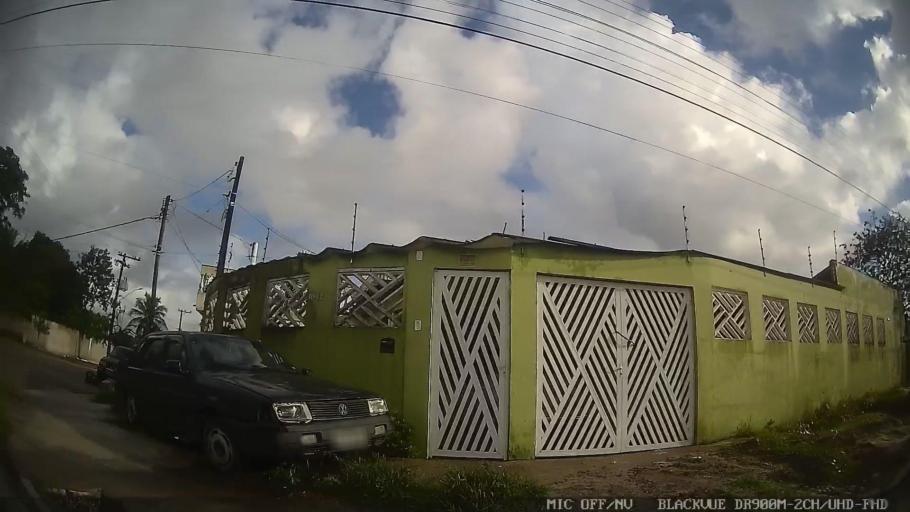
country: BR
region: Sao Paulo
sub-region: Itanhaem
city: Itanhaem
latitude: -24.1783
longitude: -46.8528
